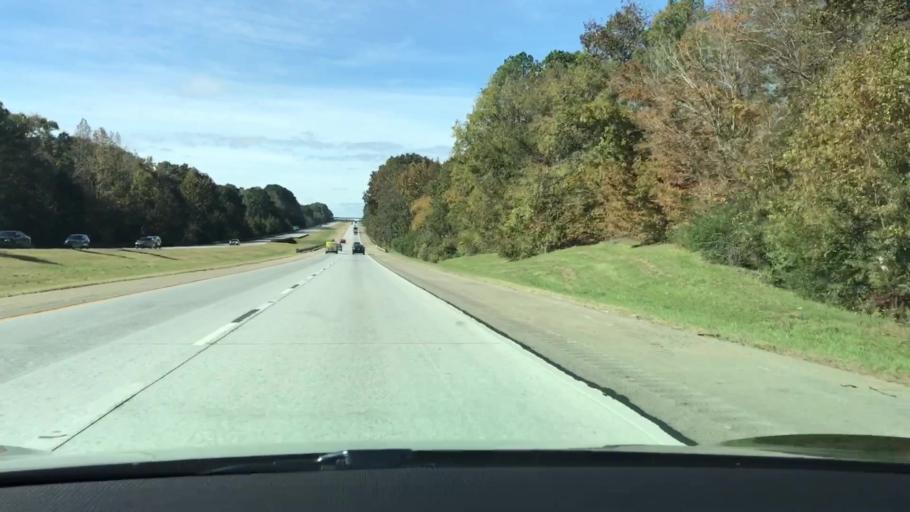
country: US
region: Georgia
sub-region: Greene County
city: Greensboro
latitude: 33.5431
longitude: -83.2209
